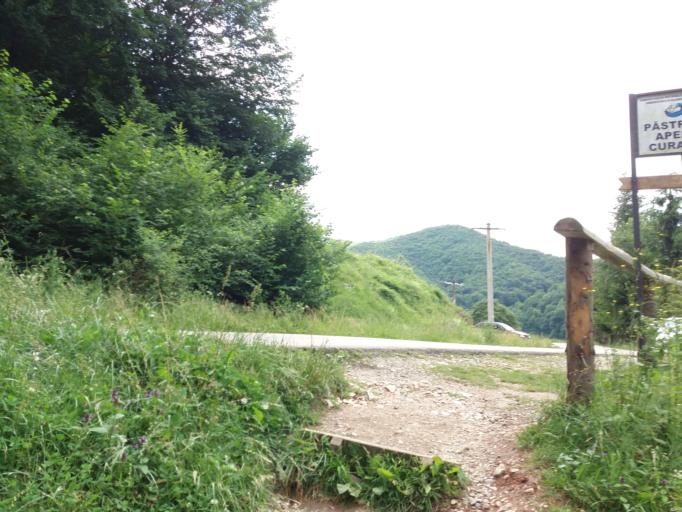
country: RO
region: Hunedoara
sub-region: Comuna Aninoasa
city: Aninoasa
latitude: 45.4536
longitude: 23.3186
